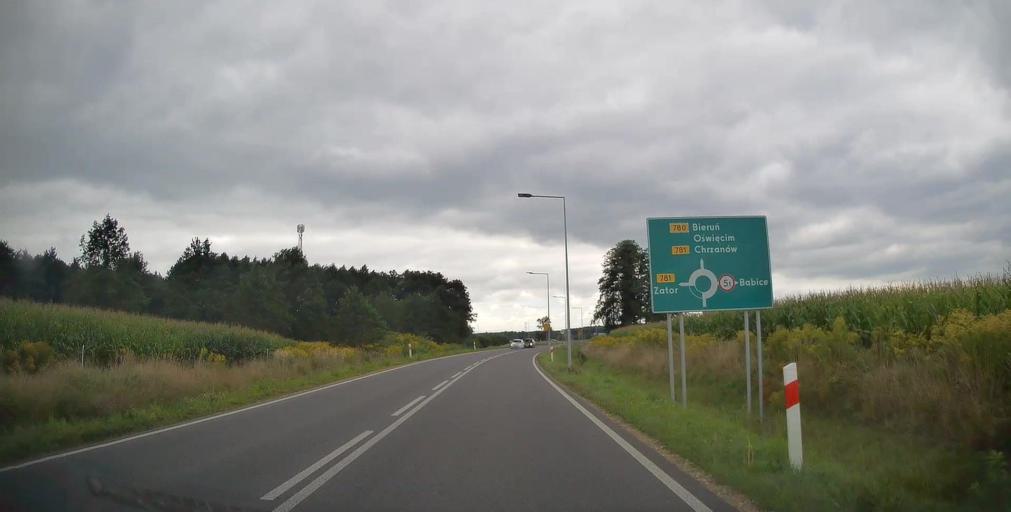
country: PL
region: Lesser Poland Voivodeship
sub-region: Powiat chrzanowski
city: Babice
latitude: 50.0625
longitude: 19.4555
